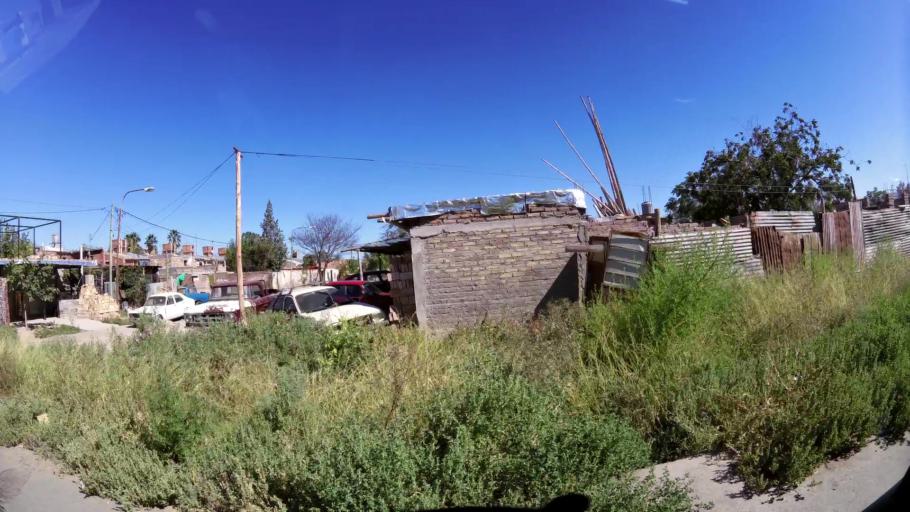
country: AR
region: Mendoza
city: Las Heras
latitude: -32.8350
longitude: -68.8183
